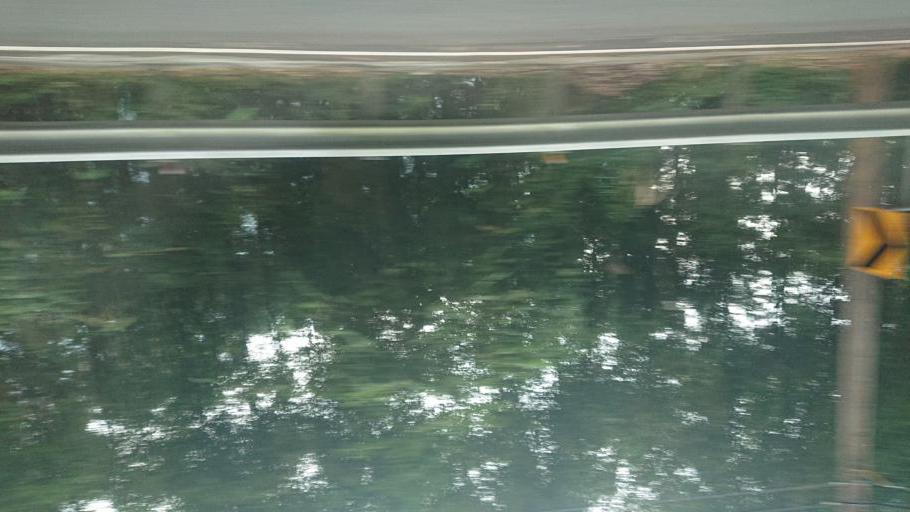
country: TW
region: Taiwan
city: Lugu
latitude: 23.4810
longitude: 120.7427
